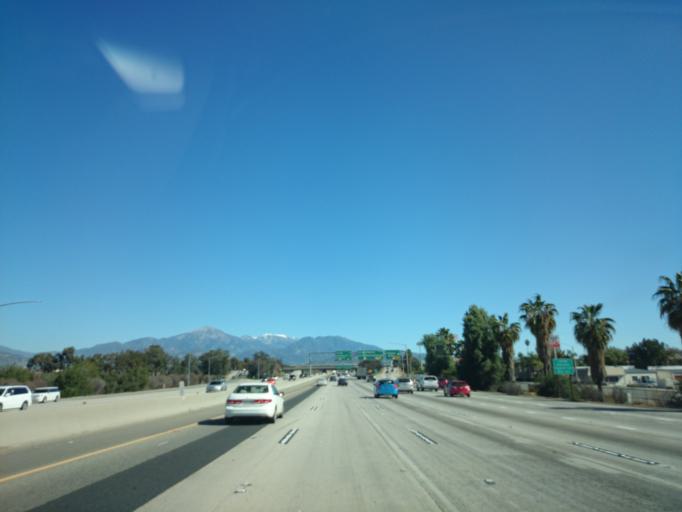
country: US
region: California
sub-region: San Bernardino County
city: Redlands
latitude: 34.0667
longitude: -117.2150
